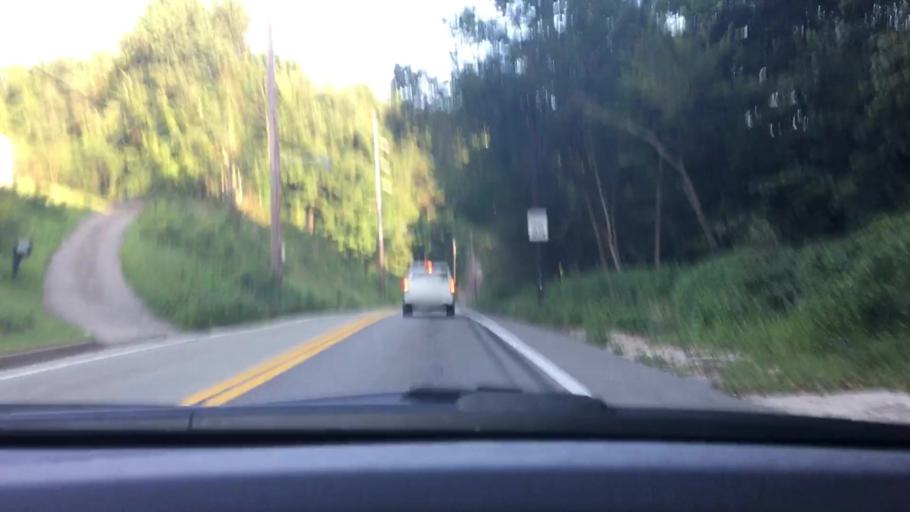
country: US
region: Pennsylvania
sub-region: Allegheny County
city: West Homestead
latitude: 40.3733
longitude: -79.9191
